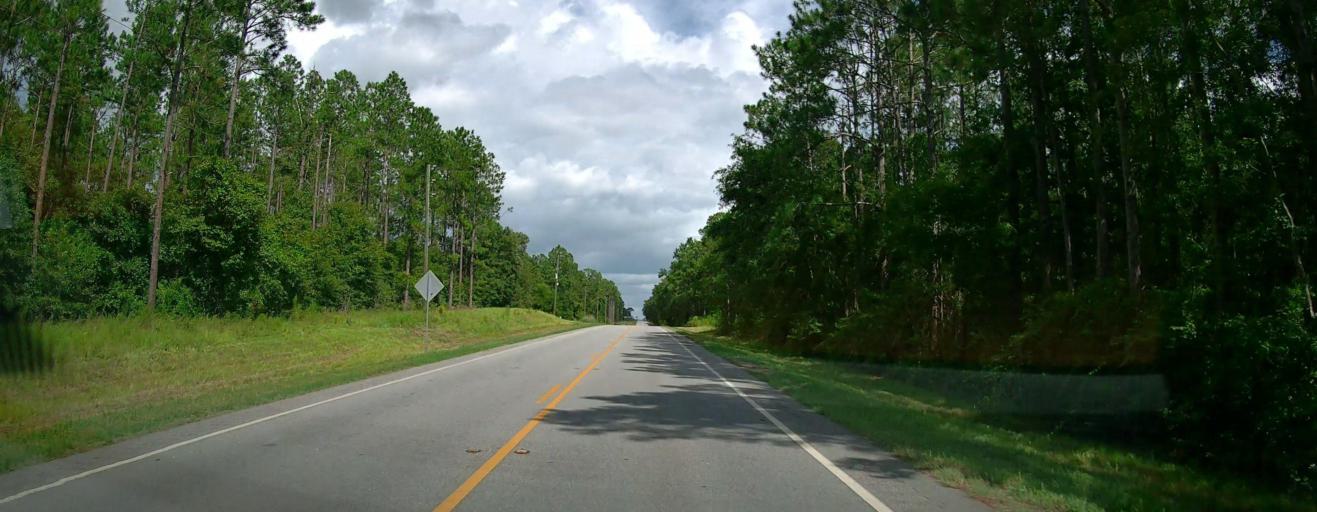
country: US
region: Georgia
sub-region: Coffee County
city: Broxton
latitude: 31.5744
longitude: -83.0384
